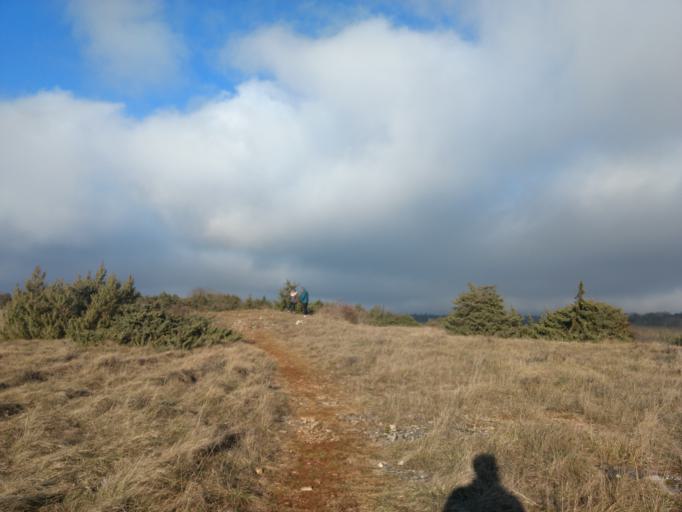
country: FR
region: Midi-Pyrenees
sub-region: Departement de l'Aveyron
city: Salles-la-Source
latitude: 44.4351
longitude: 2.5249
